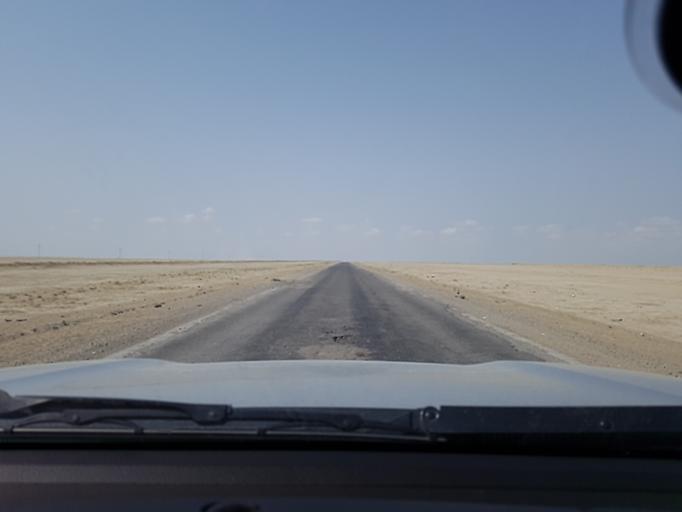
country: TM
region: Balkan
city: Gumdag
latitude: 38.6776
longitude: 54.4125
